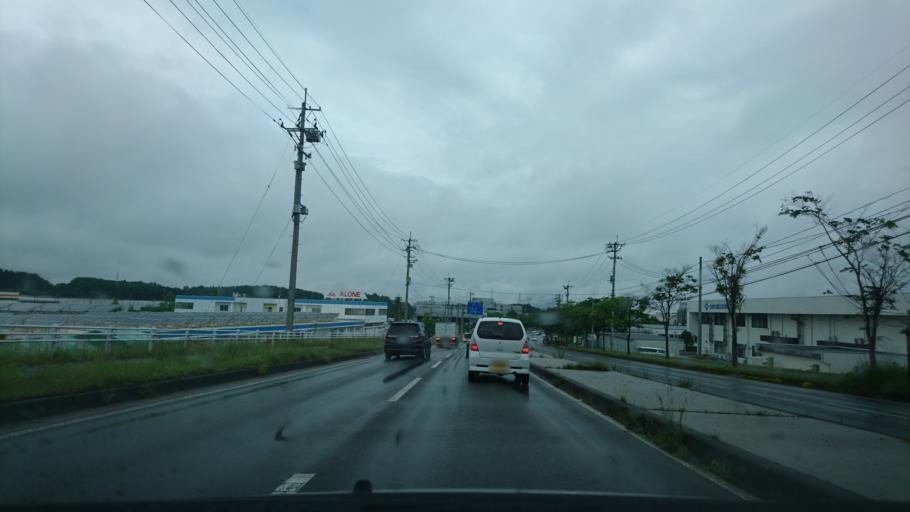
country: JP
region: Iwate
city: Ichinoseki
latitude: 38.9169
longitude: 141.1589
